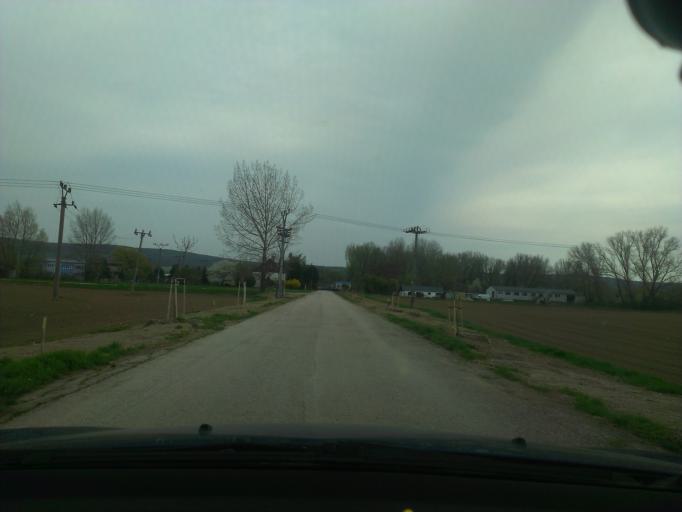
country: SK
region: Trnavsky
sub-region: Okres Trnava
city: Piestany
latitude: 48.5456
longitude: 17.8096
